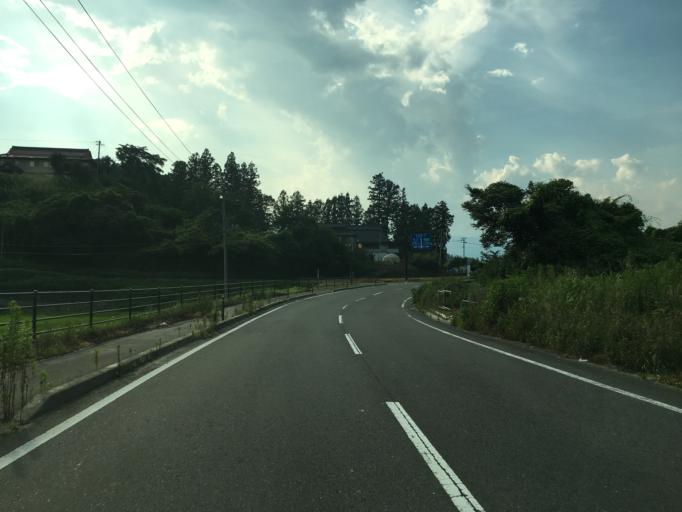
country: JP
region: Fukushima
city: Nihommatsu
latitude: 37.5513
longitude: 140.4378
